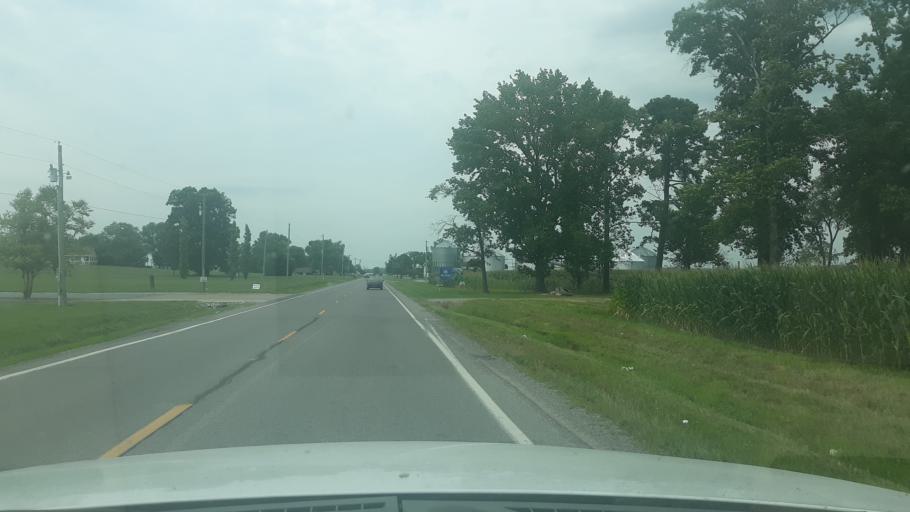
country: US
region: Illinois
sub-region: Saline County
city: Harrisburg
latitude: 37.7947
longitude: -88.5400
